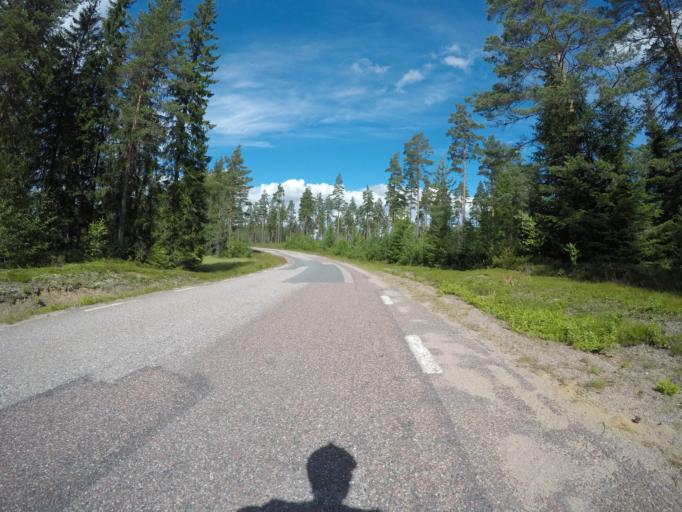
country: SE
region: OErebro
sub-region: Hallefors Kommun
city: Haellefors
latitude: 60.0873
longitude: 14.4851
